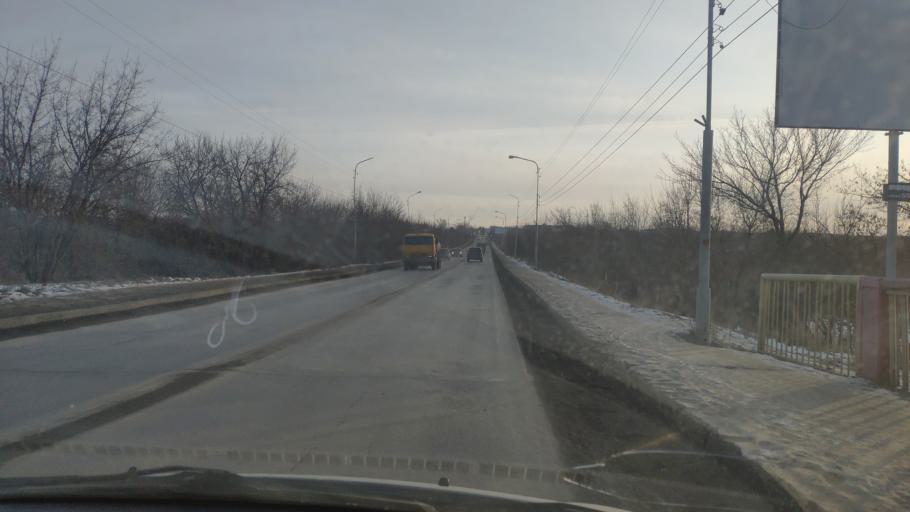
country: RU
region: Kurgan
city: Shadrinsk
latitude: 56.0746
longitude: 63.6425
